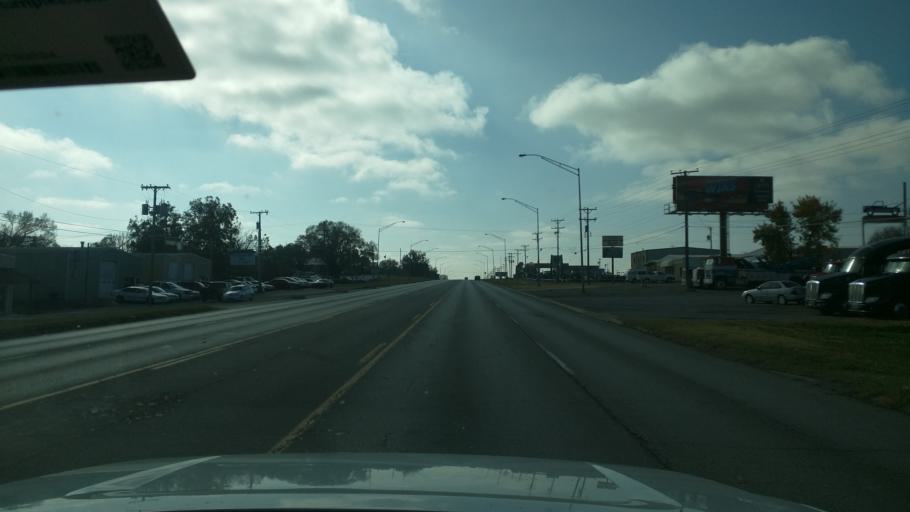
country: US
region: Oklahoma
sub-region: Washington County
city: Dewey
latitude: 36.7692
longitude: -95.9355
